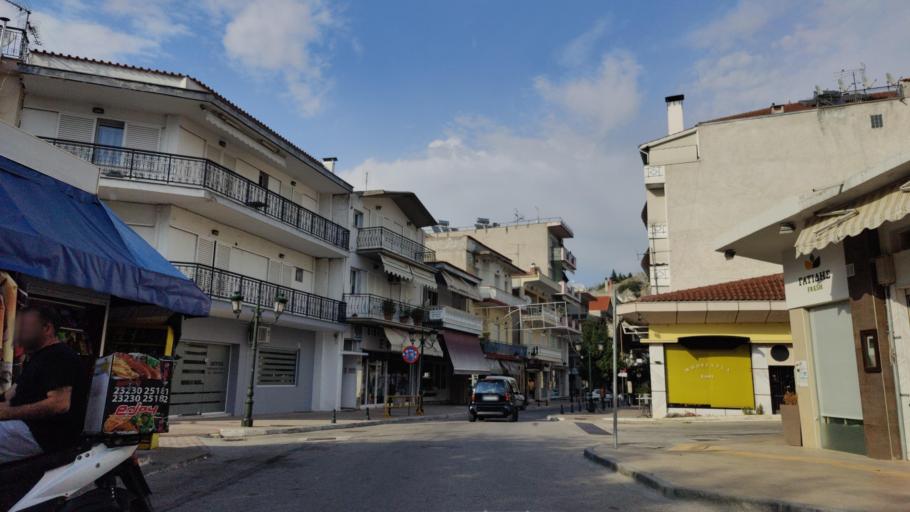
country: GR
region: Central Macedonia
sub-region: Nomos Serron
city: Sidirokastro
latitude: 41.2360
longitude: 23.3910
